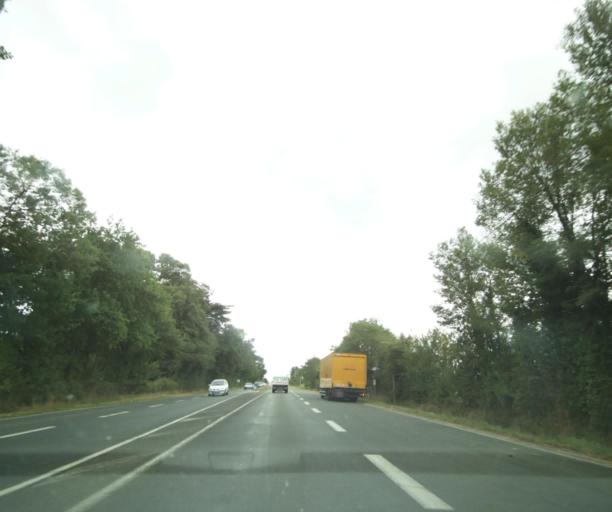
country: FR
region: Pays de la Loire
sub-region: Departement de Maine-et-Loire
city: Durtal
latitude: 47.6393
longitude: -0.2832
